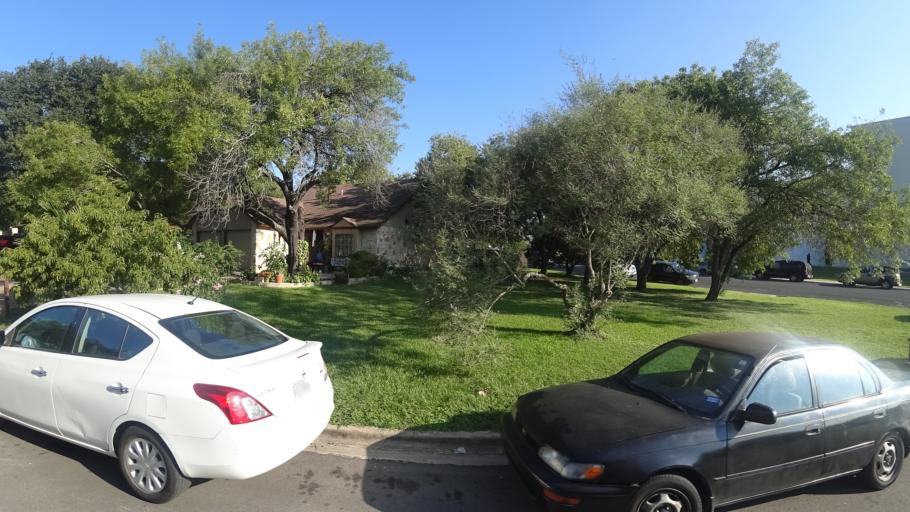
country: US
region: Texas
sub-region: Travis County
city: Austin
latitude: 30.3121
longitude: -97.6583
